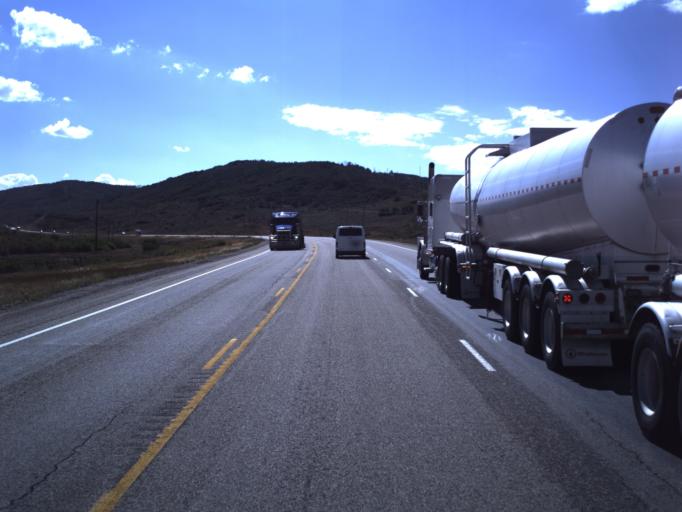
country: US
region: Utah
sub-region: Summit County
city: Francis
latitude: 40.1997
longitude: -110.9960
